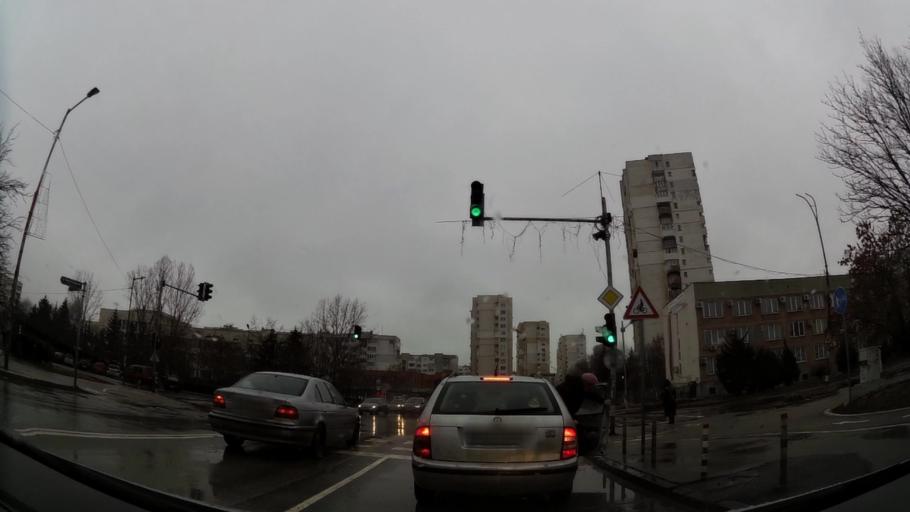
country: BG
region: Sofia-Capital
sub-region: Stolichna Obshtina
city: Sofia
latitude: 42.6411
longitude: 23.3814
